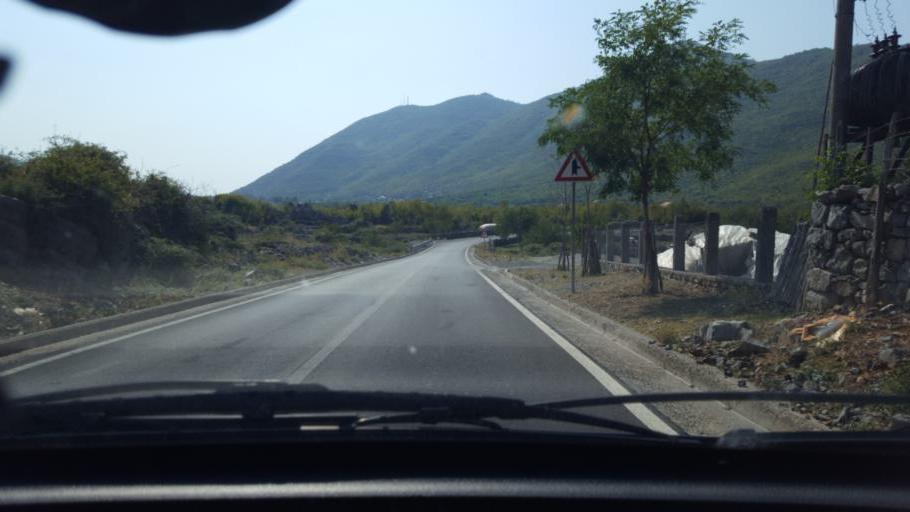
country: AL
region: Shkoder
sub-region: Rrethi i Malesia e Madhe
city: Kastrat
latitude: 42.4085
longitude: 19.5023
